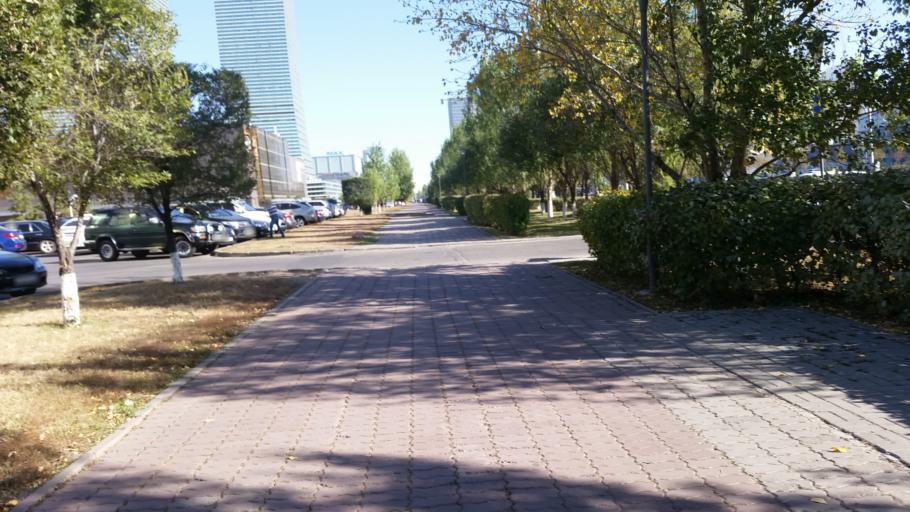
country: KZ
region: Astana Qalasy
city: Astana
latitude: 51.1281
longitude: 71.4172
